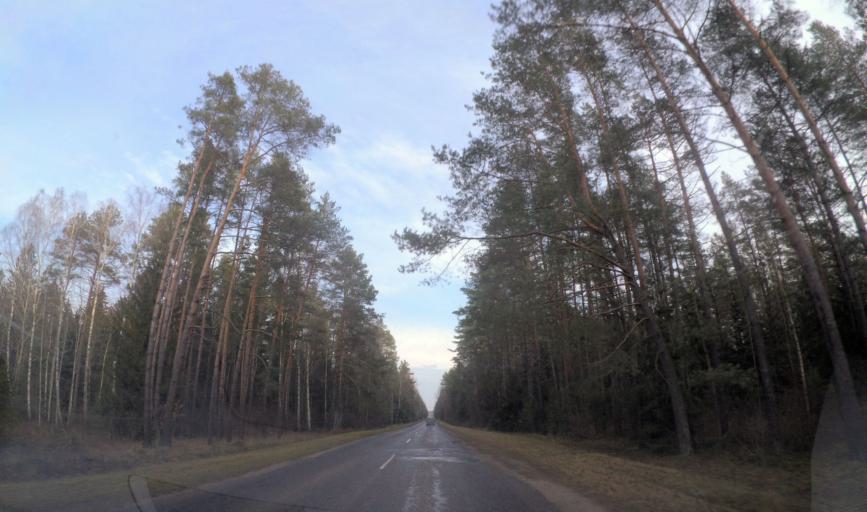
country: LT
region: Alytaus apskritis
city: Druskininkai
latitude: 53.8182
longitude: 24.0446
